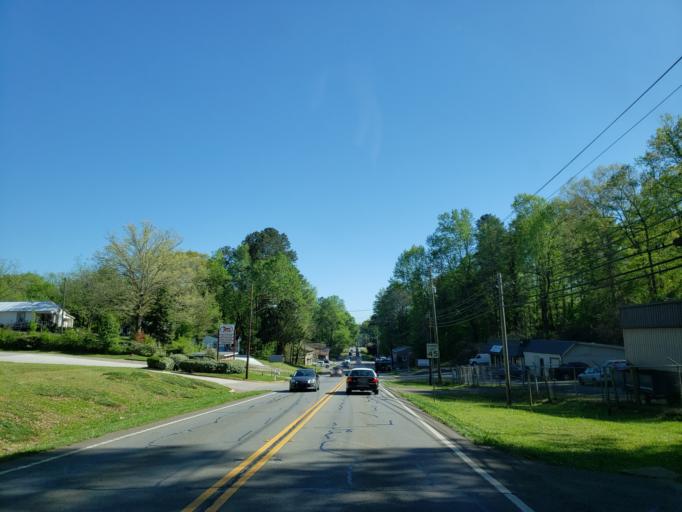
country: US
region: Georgia
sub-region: Cherokee County
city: Canton
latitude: 34.2514
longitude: -84.4939
